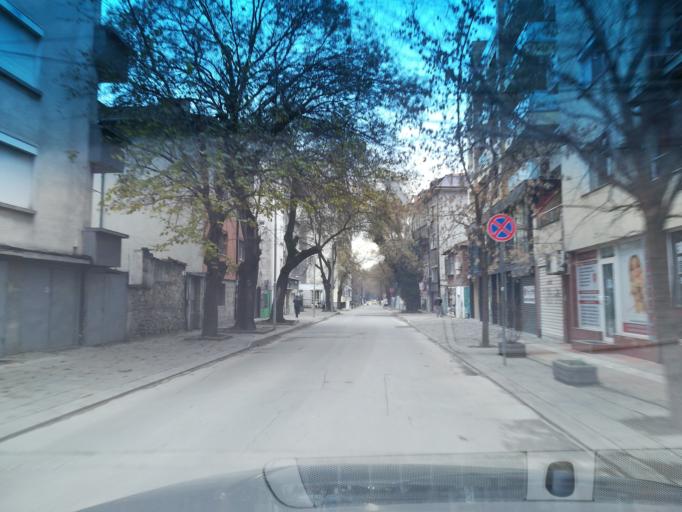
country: BG
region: Plovdiv
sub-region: Obshtina Plovdiv
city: Plovdiv
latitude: 42.1440
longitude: 24.7587
